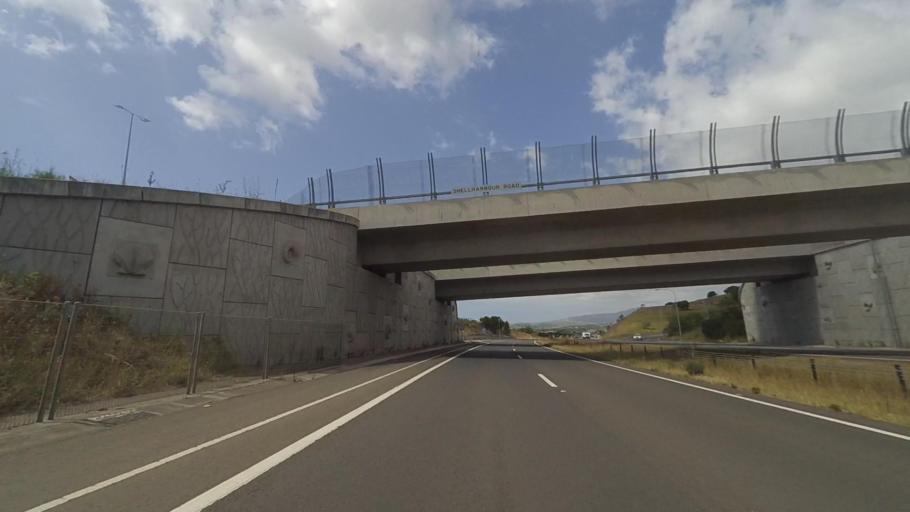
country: AU
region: New South Wales
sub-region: Shellharbour
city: Croom
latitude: -34.5885
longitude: 150.8447
